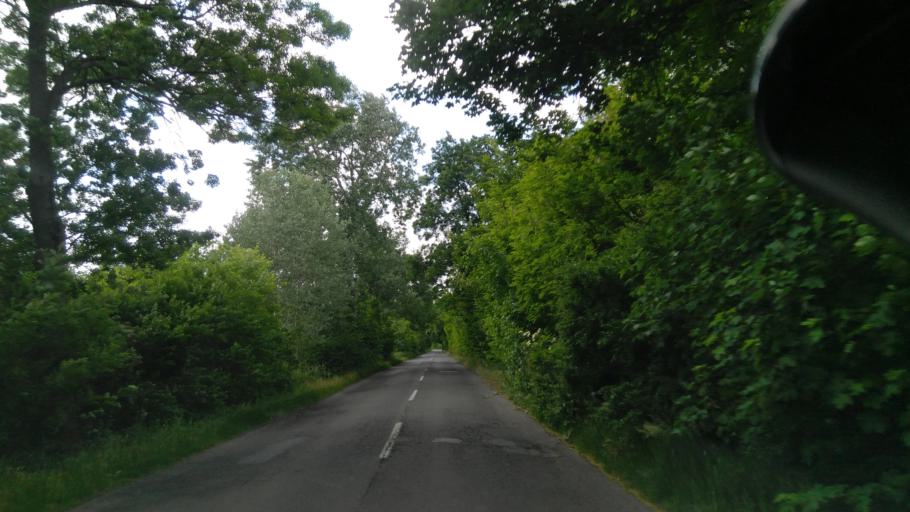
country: HU
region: Bekes
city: Bucsa
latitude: 47.1667
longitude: 21.0825
